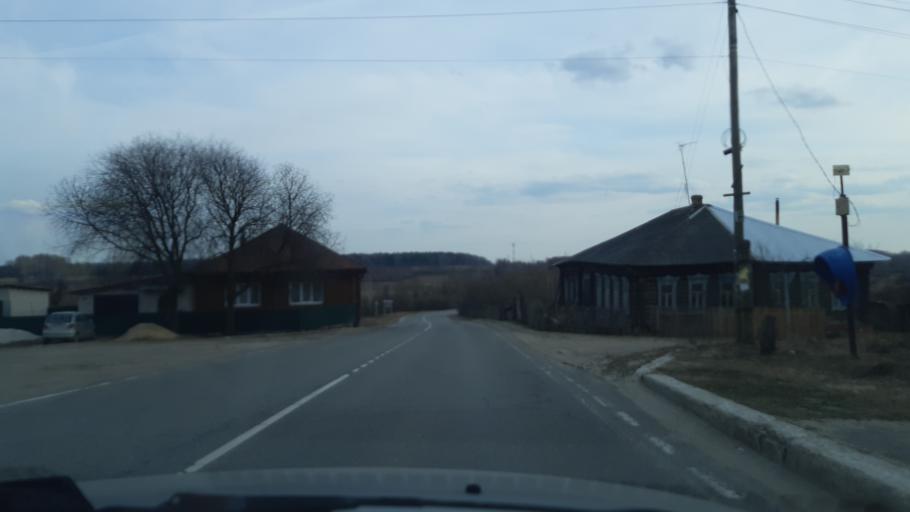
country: RU
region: Vladimir
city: Luknovo
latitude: 56.2146
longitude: 42.0301
